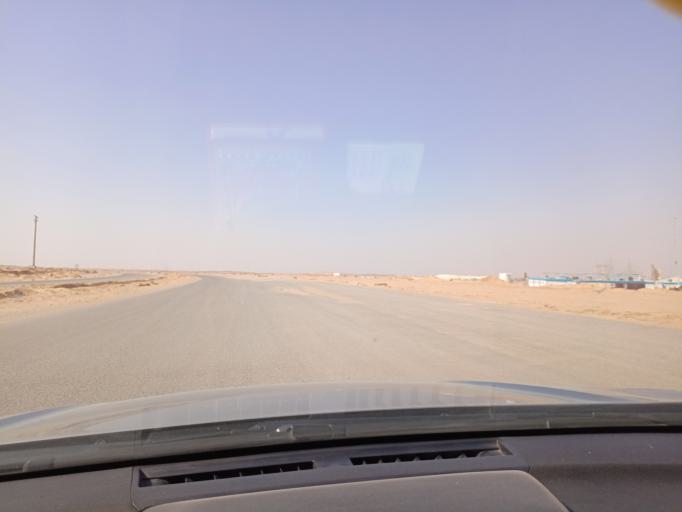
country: EG
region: Muhafazat al Qalyubiyah
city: Al Khankah
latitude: 30.0383
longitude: 31.7164
